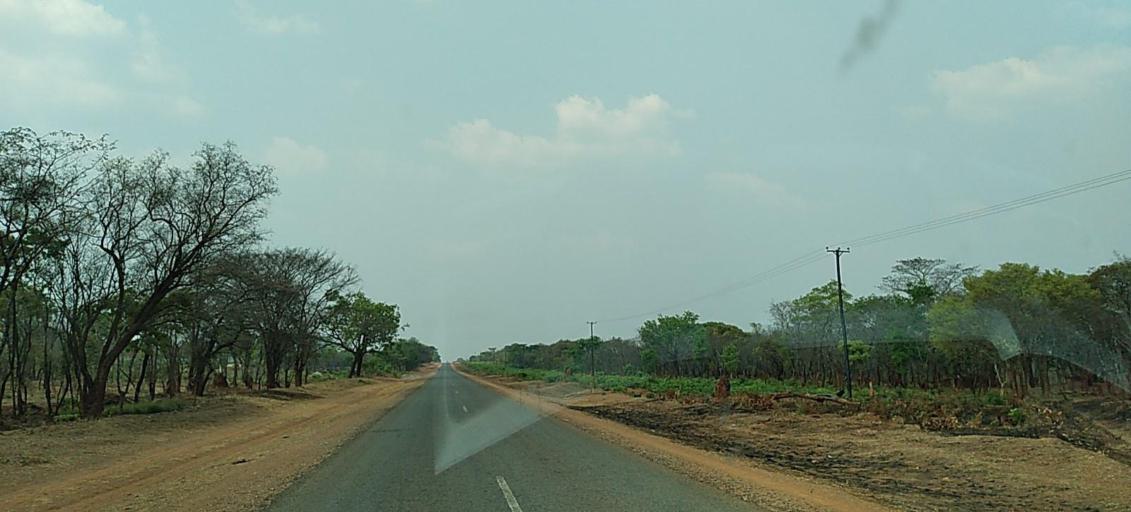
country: ZM
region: North-Western
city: Kabompo
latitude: -13.5763
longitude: 24.2398
